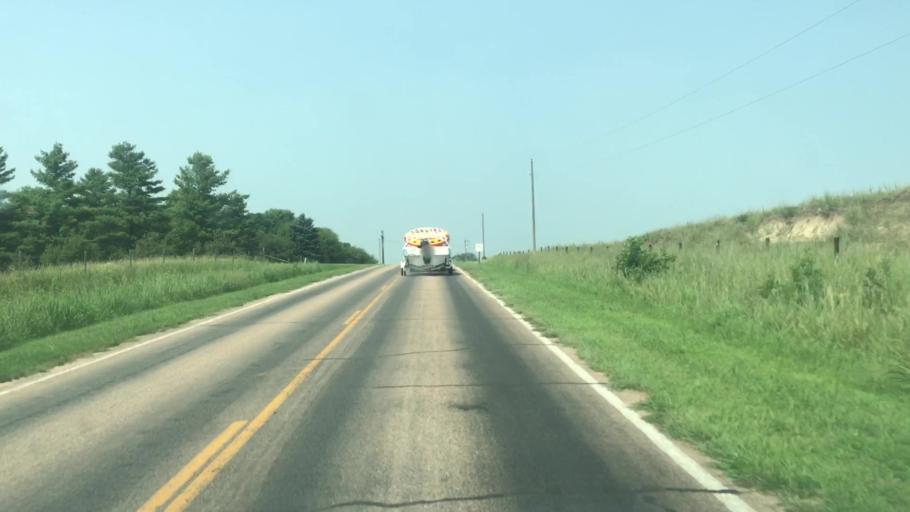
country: US
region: Nebraska
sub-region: Sherman County
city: Loup City
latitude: 41.2840
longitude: -98.8998
